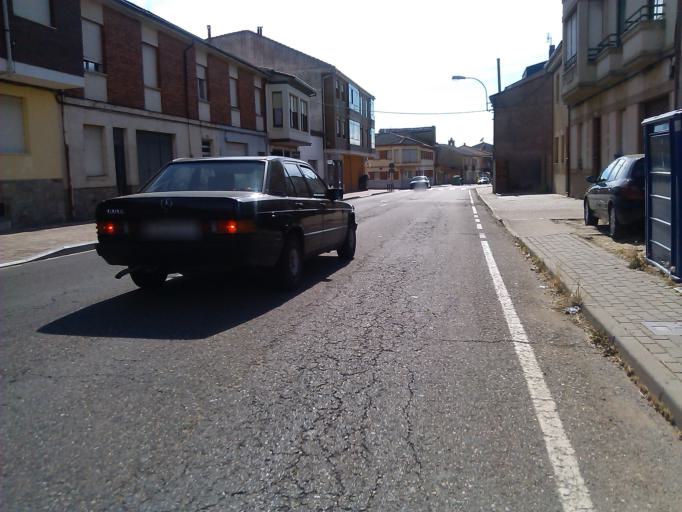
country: ES
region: Castille and Leon
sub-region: Provincia de Leon
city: San Justo de la Vega
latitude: 42.4542
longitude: -6.0137
